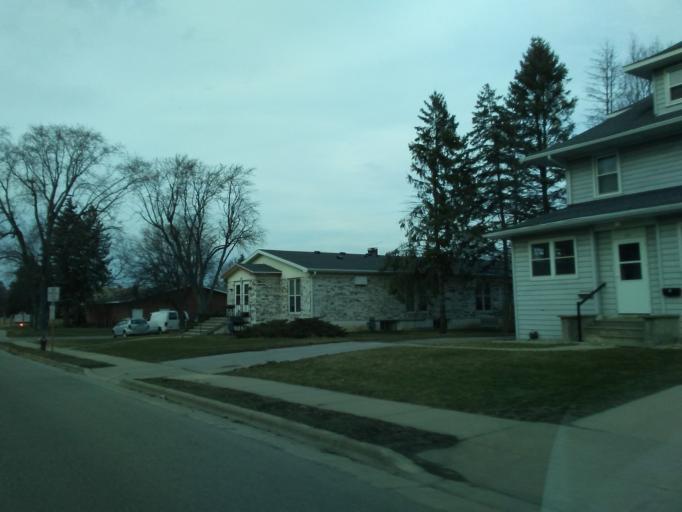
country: US
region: Wisconsin
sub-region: Dane County
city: Verona
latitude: 42.9928
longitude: -89.5335
